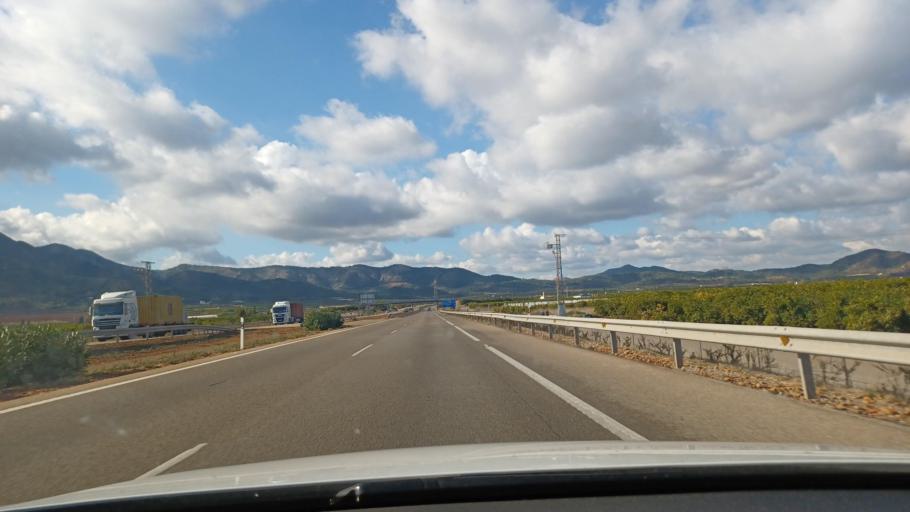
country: ES
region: Valencia
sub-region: Provincia de Castello
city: Villavieja
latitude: 39.8665
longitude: -0.1750
